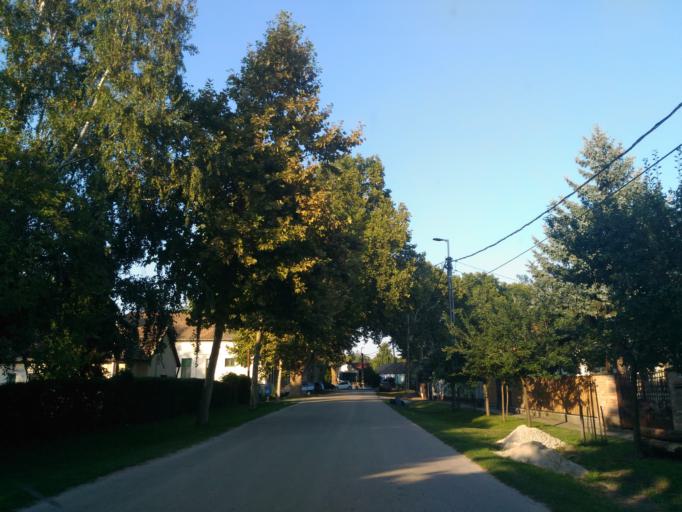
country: HU
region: Somogy
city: Balatonszarszo
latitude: 46.8091
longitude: 17.7719
